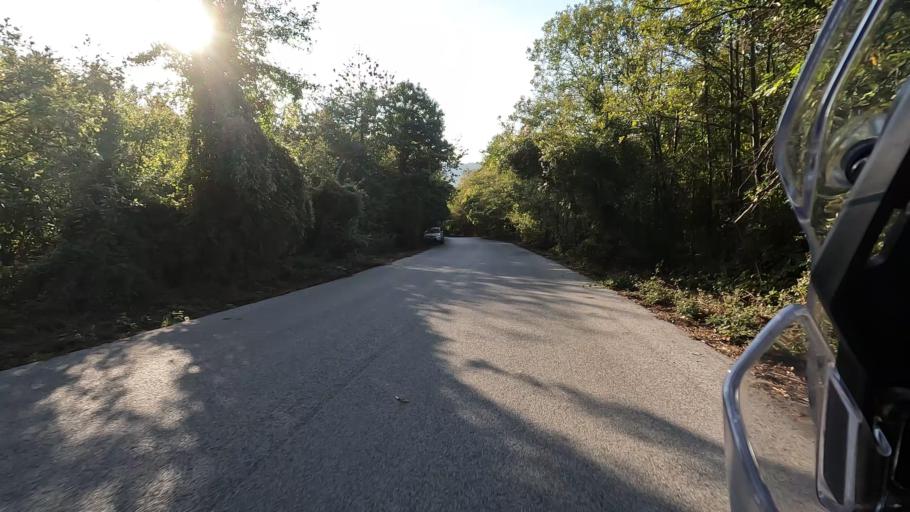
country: IT
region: Liguria
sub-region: Provincia di Savona
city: San Giovanni
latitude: 44.4147
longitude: 8.5257
